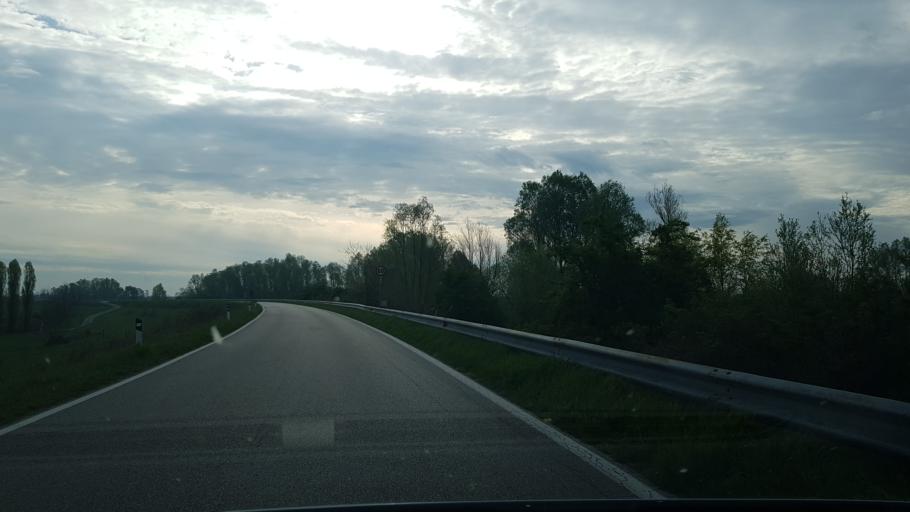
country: IT
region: Veneto
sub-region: Provincia di Padova
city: Barbona
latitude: 45.0982
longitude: 11.7230
